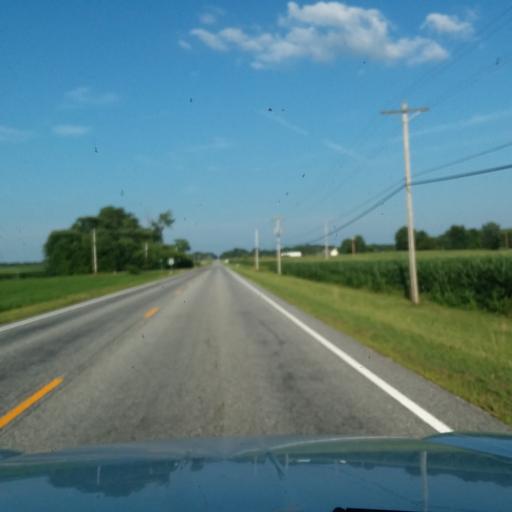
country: US
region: Indiana
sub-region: Johnson County
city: Franklin
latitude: 39.4117
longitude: -86.0330
